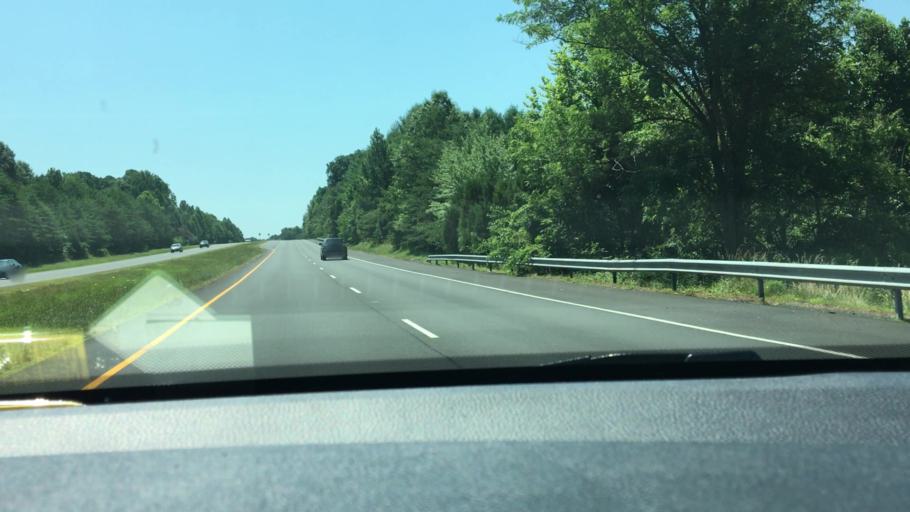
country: US
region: Virginia
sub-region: Prince William County
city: Buckhall
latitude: 38.7261
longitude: -77.4215
